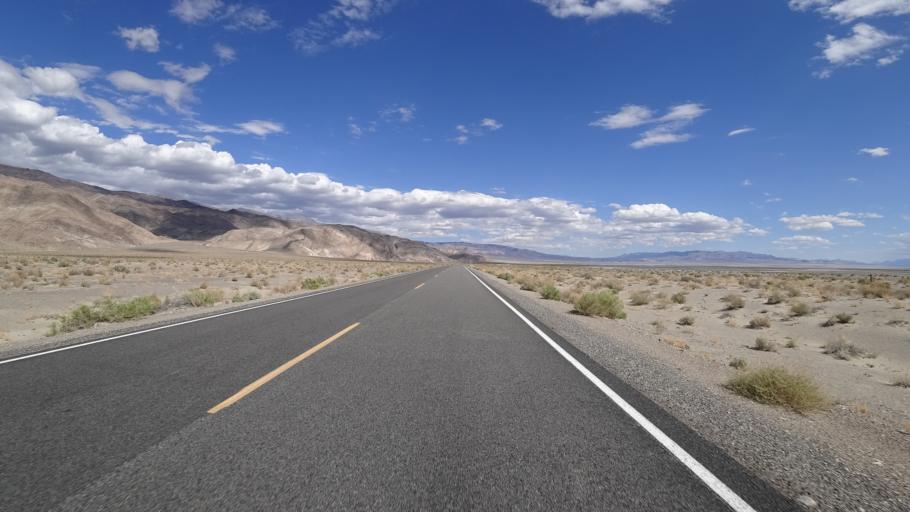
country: US
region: California
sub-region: Inyo County
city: Lone Pine
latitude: 36.5500
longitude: -117.9490
